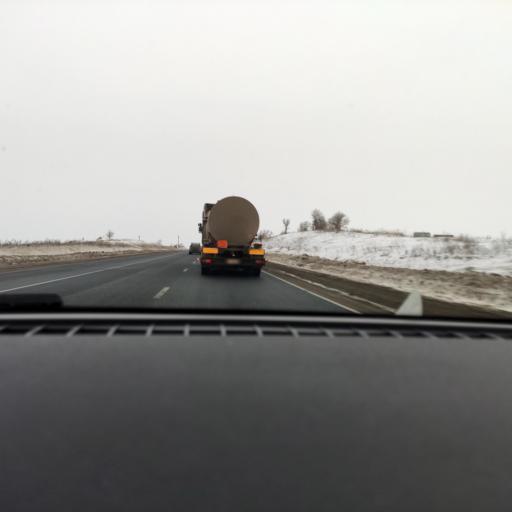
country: RU
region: Samara
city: Novosemeykino
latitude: 53.3874
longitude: 50.4290
